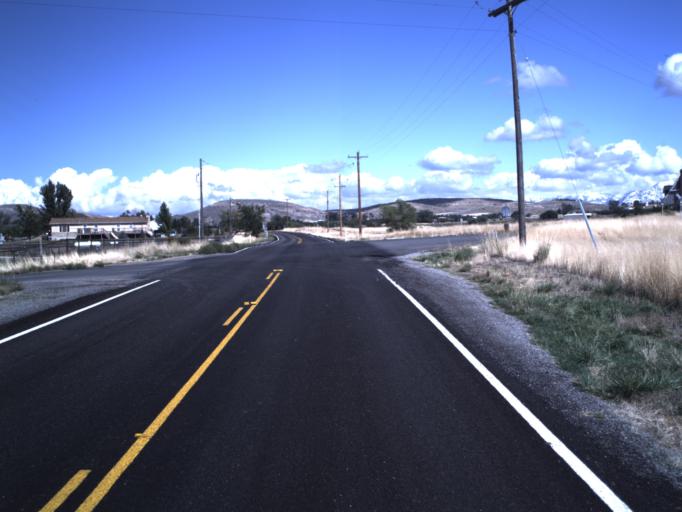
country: US
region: Utah
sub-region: Utah County
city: Genola
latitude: 39.9816
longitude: -111.8413
